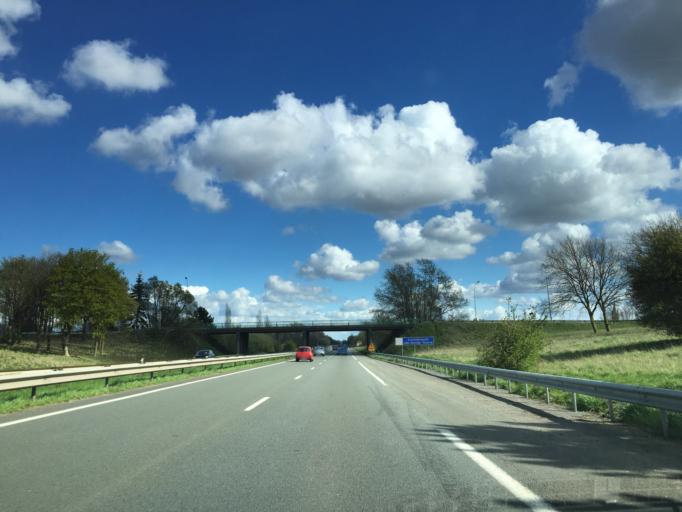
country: FR
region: Nord-Pas-de-Calais
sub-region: Departement du Nord
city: Erquinghem-Lys
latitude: 50.6844
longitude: 2.8393
